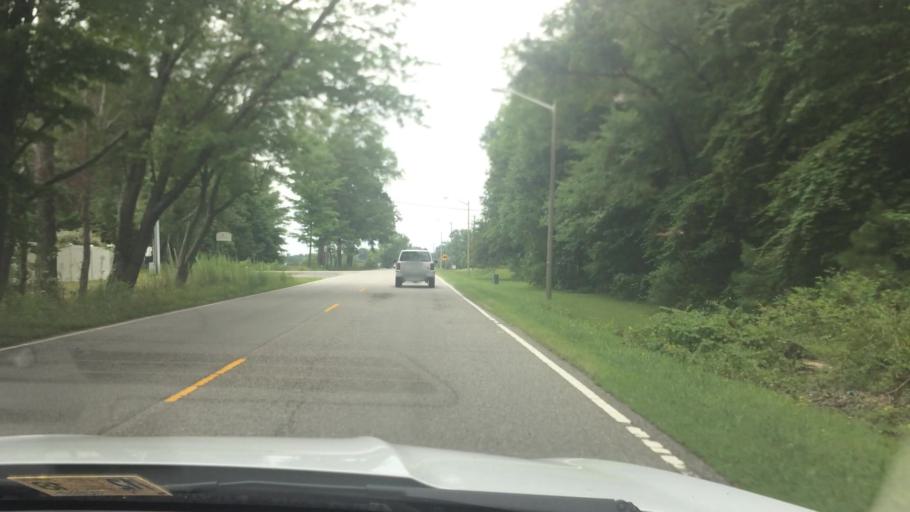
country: US
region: Virginia
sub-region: York County
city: Yorktown
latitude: 37.2159
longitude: -76.5690
